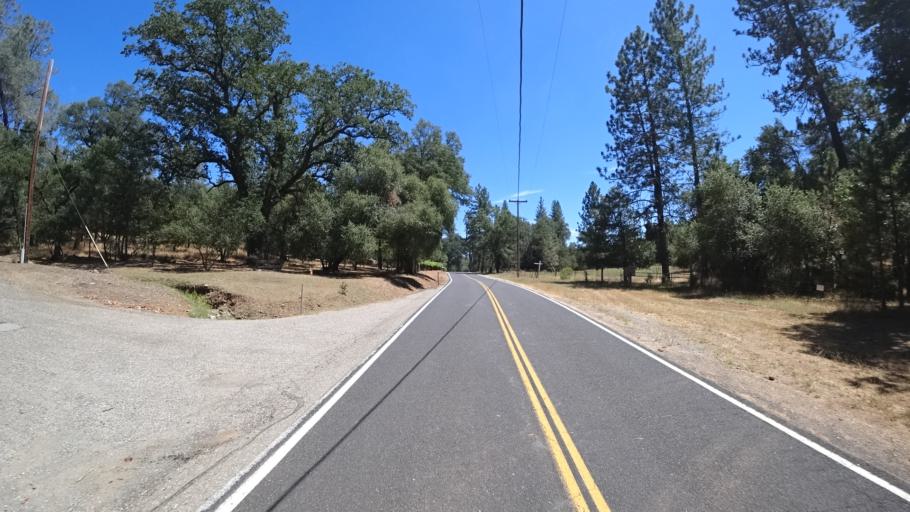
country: US
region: California
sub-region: Calaveras County
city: Mountain Ranch
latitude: 38.2292
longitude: -120.4945
